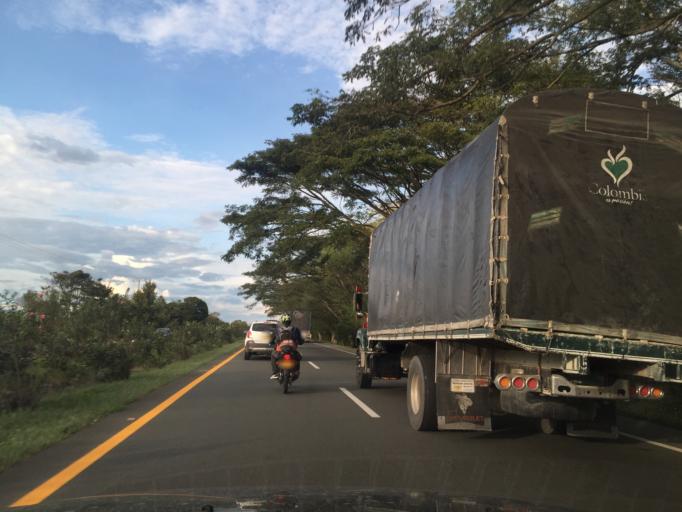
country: CO
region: Valle del Cauca
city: Andalucia
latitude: 4.1813
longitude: -76.1704
